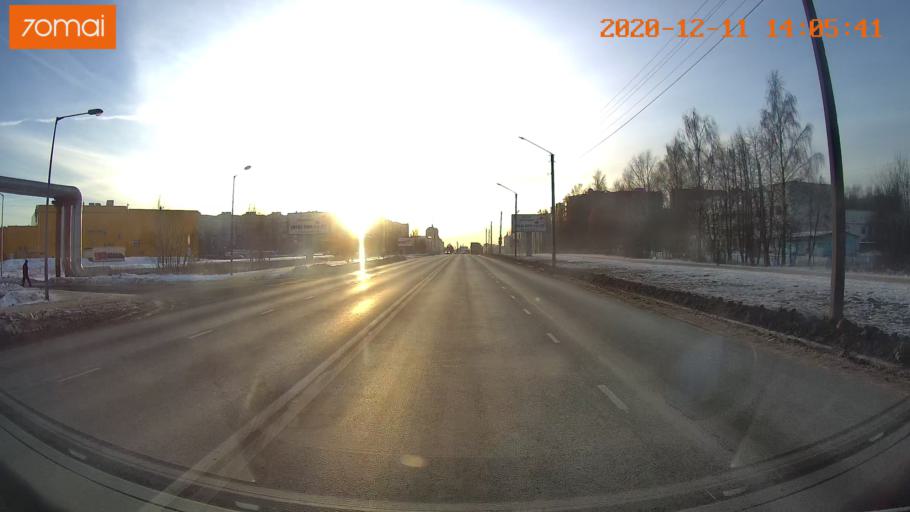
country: RU
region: Kostroma
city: Oktyabr'skiy
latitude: 57.7465
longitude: 41.0110
